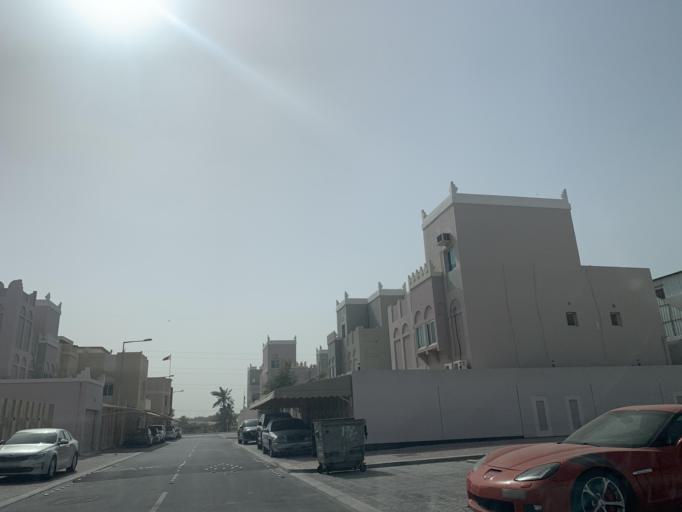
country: BH
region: Northern
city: Madinat `Isa
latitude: 26.1657
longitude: 50.5375
